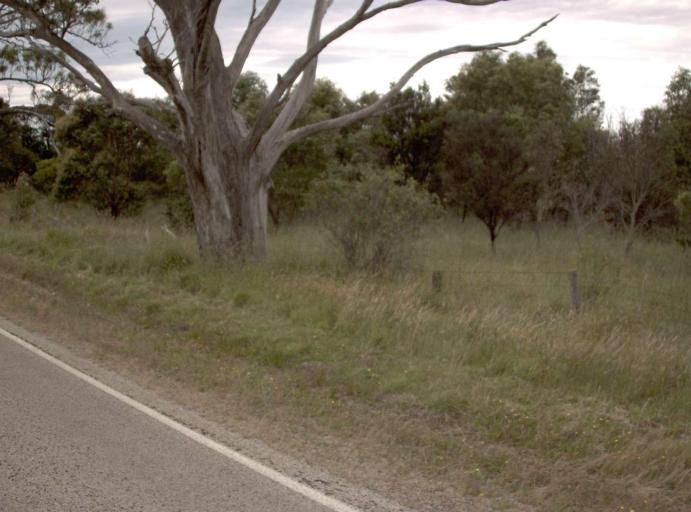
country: AU
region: Victoria
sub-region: East Gippsland
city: Bairnsdale
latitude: -37.9076
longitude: 147.5514
